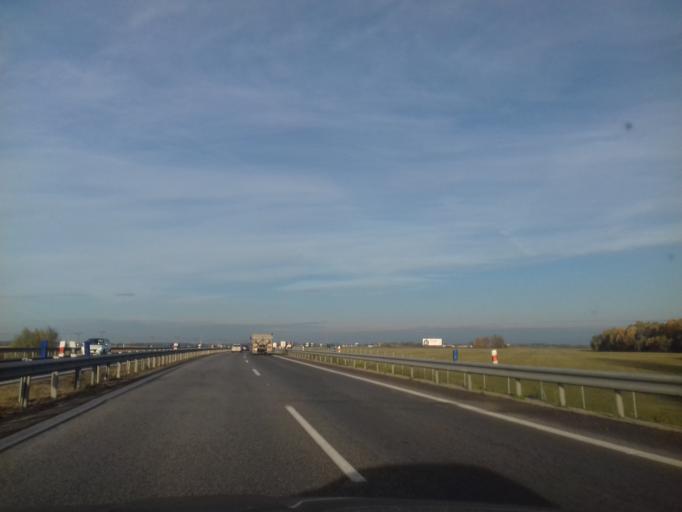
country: SK
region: Trnavsky
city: Sladkovicovo
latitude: 48.2885
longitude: 17.6918
